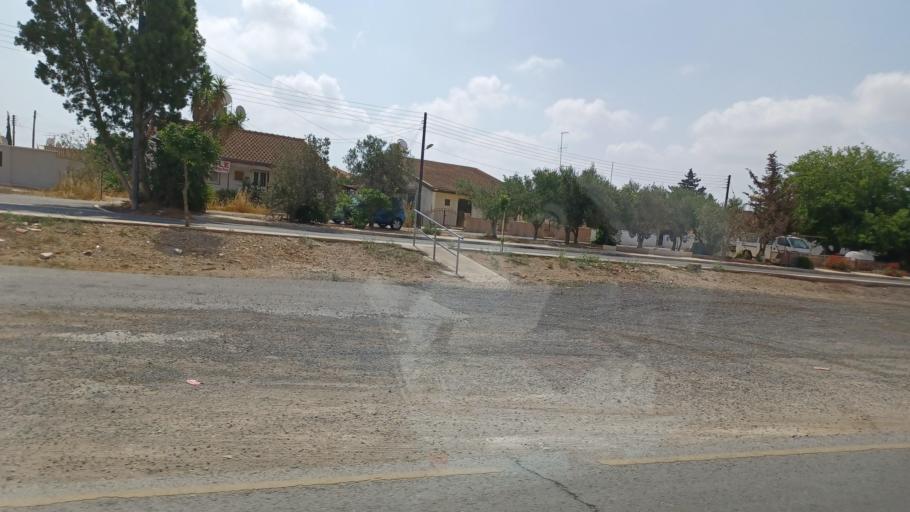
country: CY
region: Ammochostos
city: Deryneia
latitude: 35.0495
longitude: 33.9571
